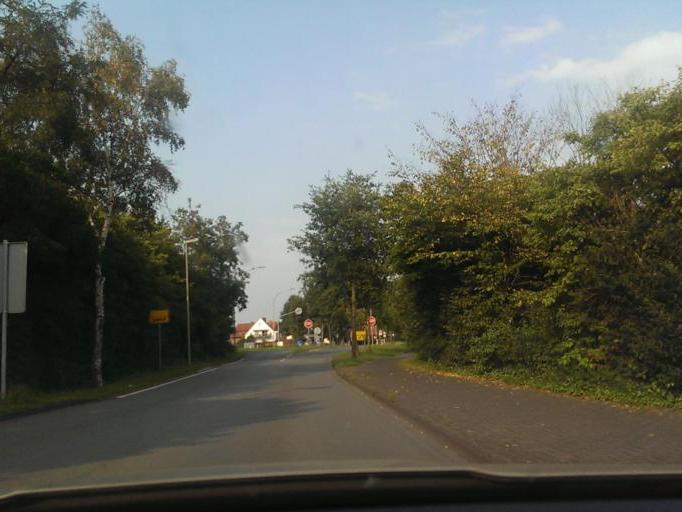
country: DE
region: North Rhine-Westphalia
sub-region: Regierungsbezirk Detmold
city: Delbruck
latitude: 51.7695
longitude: 8.5744
